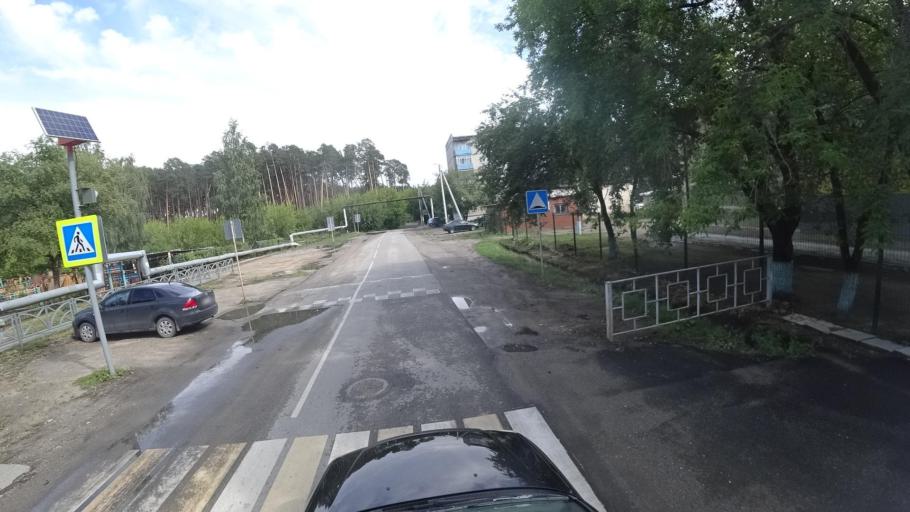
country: RU
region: Sverdlovsk
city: Kamyshlov
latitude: 56.8351
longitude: 62.7332
